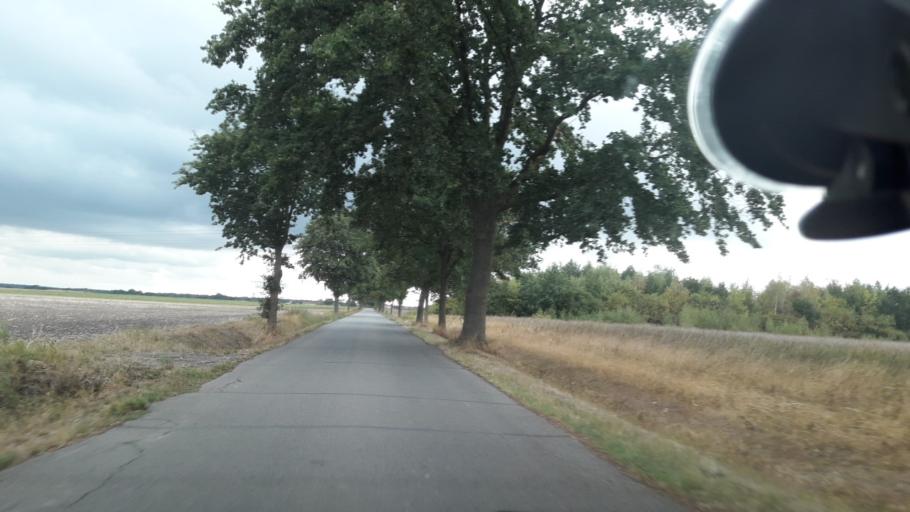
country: DE
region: Saxony-Anhalt
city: Oebisfelde
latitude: 52.4097
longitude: 10.9920
